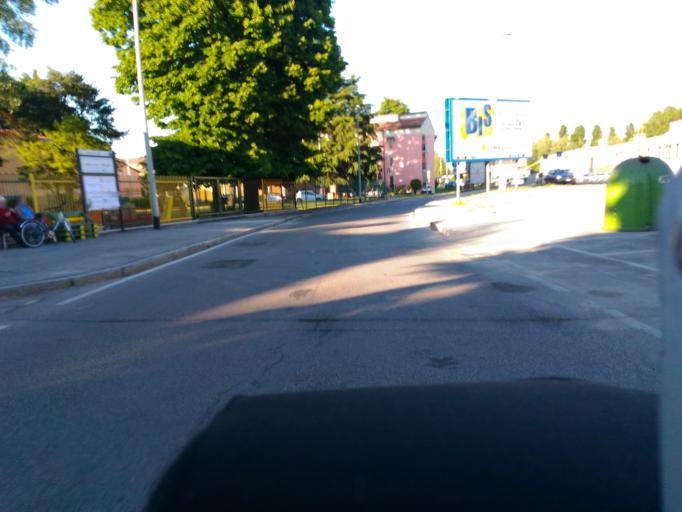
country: IT
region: Lombardy
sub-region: Provincia di Lodi
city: Lodi
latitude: 45.3256
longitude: 9.5143
